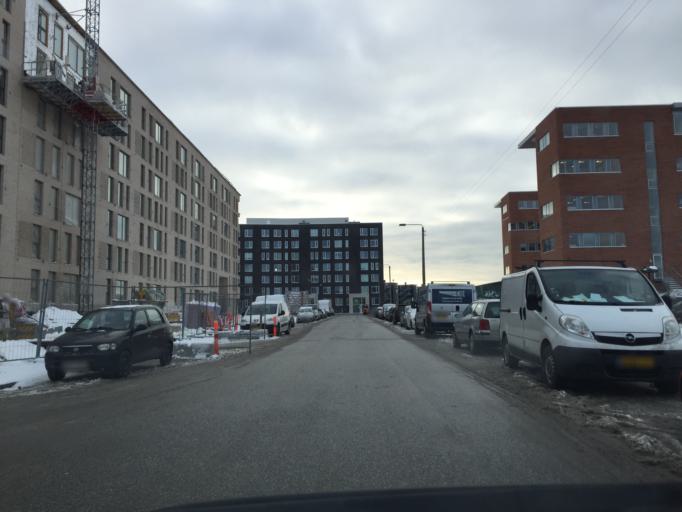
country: DK
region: Capital Region
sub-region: Kobenhavn
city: Copenhagen
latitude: 55.6536
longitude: 12.5479
